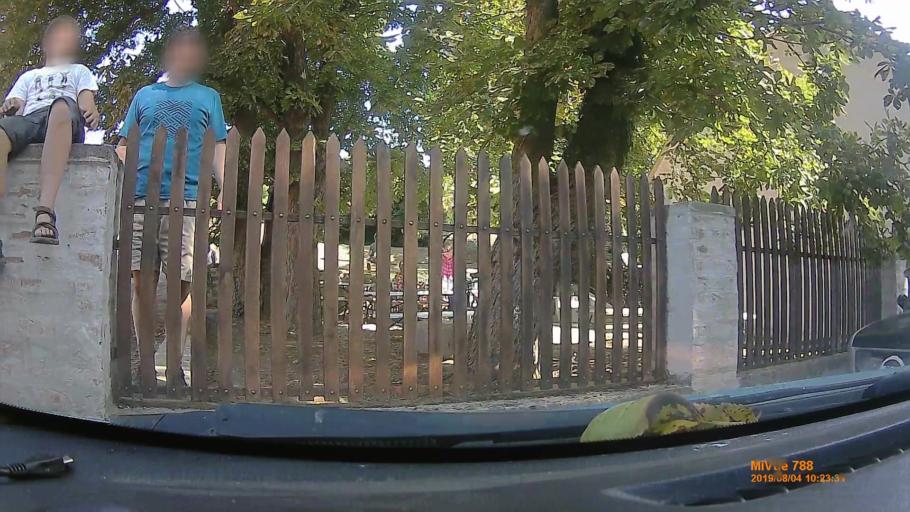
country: HU
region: Baranya
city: Buekkoesd
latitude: 46.1062
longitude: 18.0194
